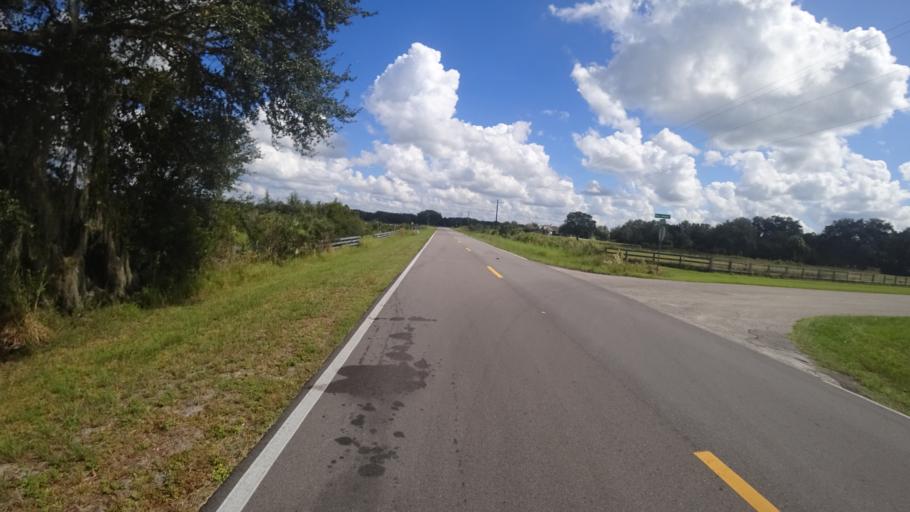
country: US
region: Florida
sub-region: Sarasota County
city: Lake Sarasota
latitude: 27.2889
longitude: -82.2237
